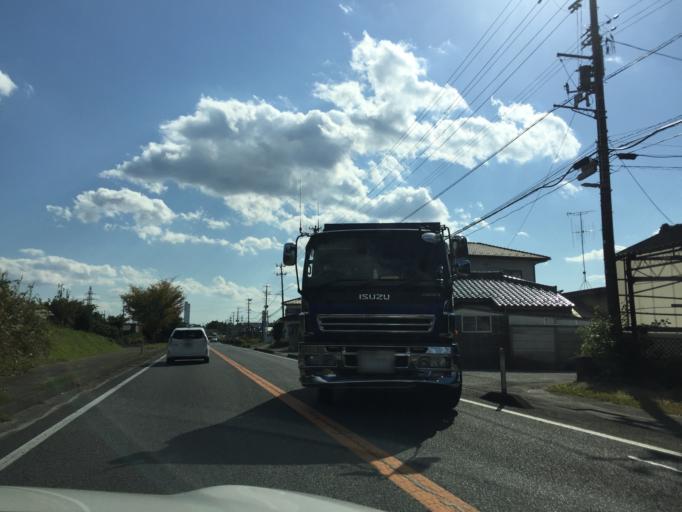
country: JP
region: Fukushima
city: Namie
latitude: 37.2646
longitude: 140.9964
